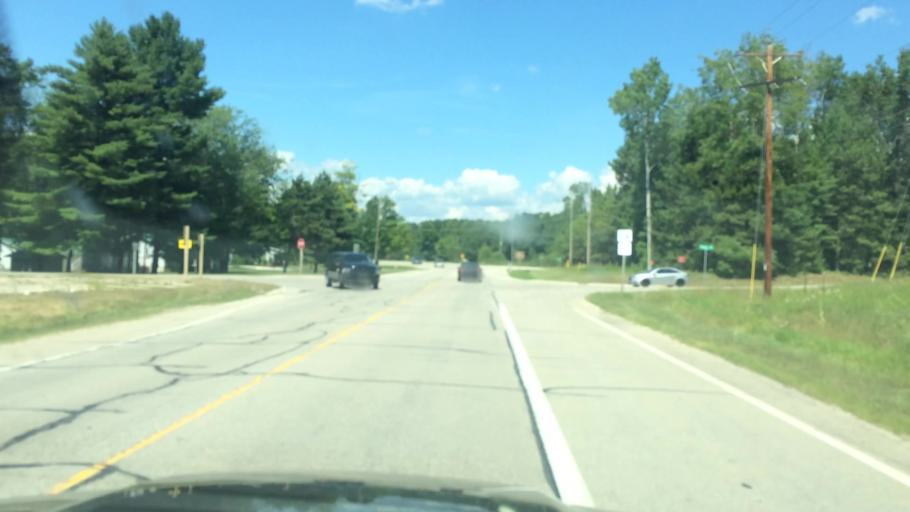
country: US
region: Wisconsin
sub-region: Marinette County
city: Peshtigo
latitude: 45.1047
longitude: -87.7498
